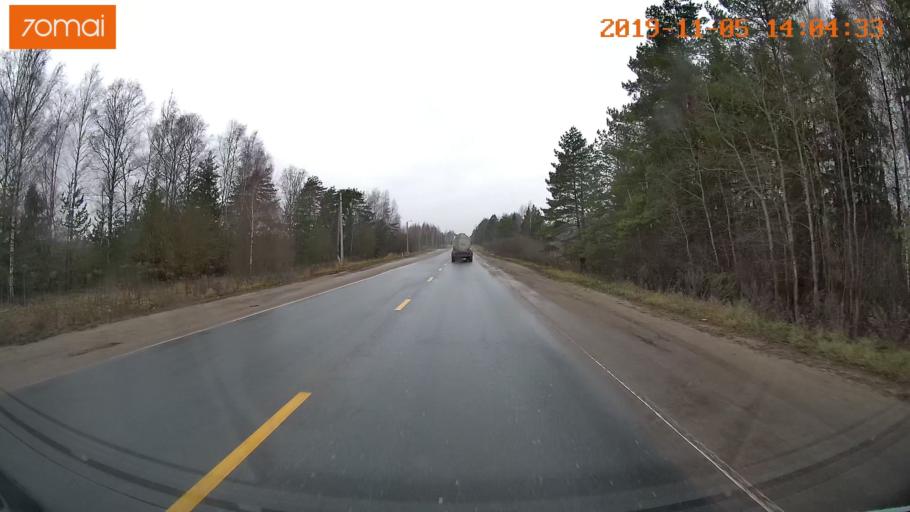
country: RU
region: Ivanovo
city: Kokhma
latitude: 56.9974
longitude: 41.1741
